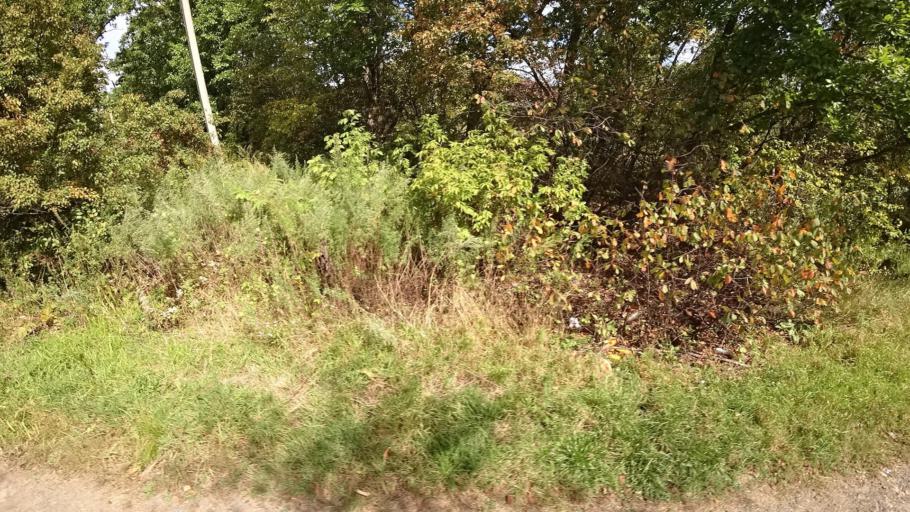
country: RU
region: Primorskiy
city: Yakovlevka
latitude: 44.6484
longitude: 133.5915
